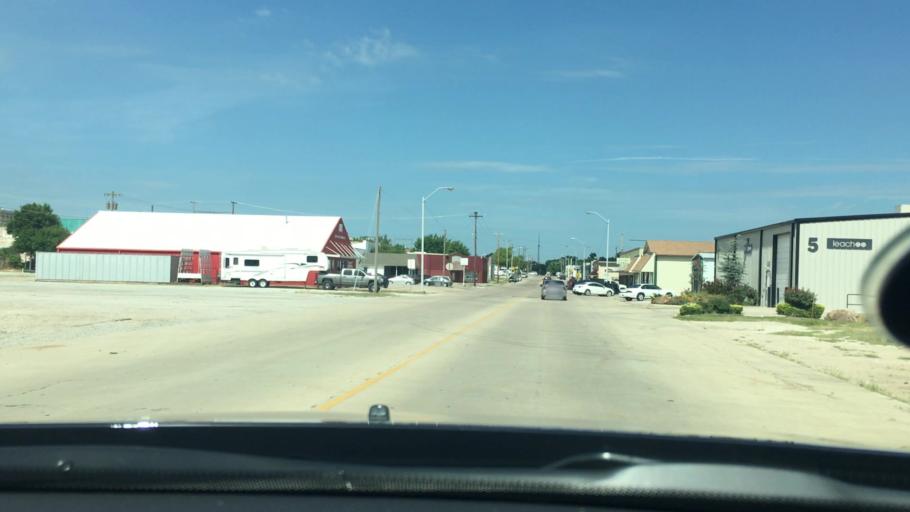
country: US
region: Oklahoma
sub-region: Pontotoc County
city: Ada
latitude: 34.7756
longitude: -96.6736
